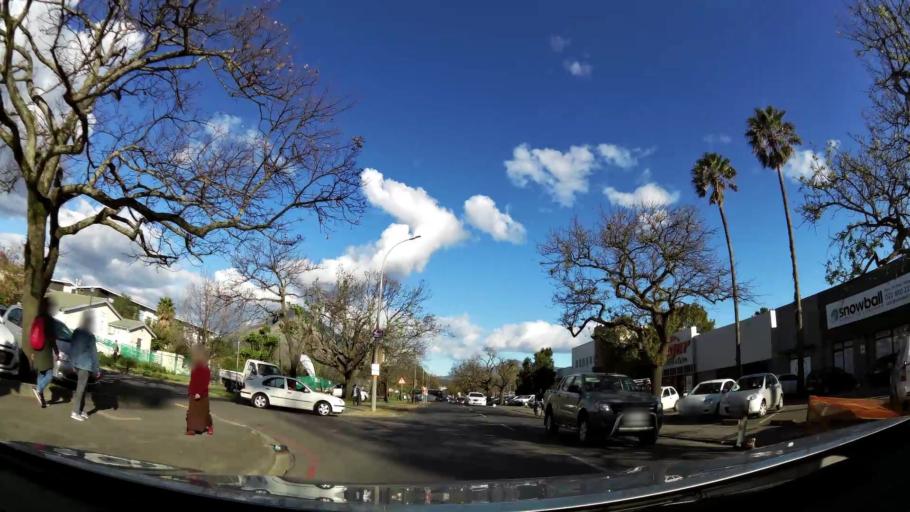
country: ZA
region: Western Cape
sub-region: Cape Winelands District Municipality
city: Stellenbosch
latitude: -33.9261
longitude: 18.8561
